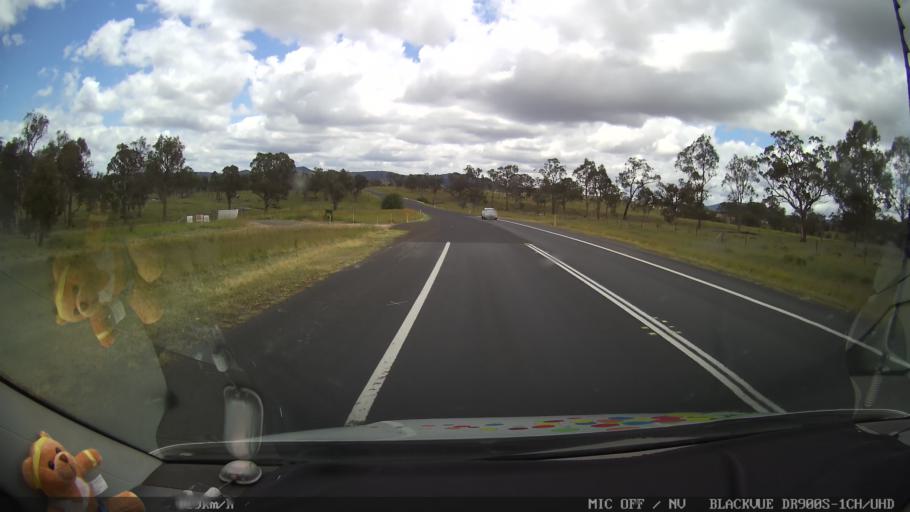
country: AU
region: New South Wales
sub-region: Glen Innes Severn
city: Glen Innes
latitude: -29.3887
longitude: 151.8878
